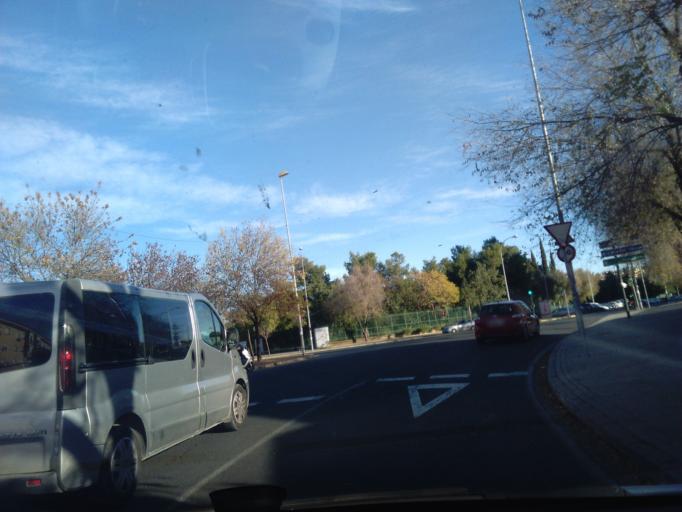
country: ES
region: Andalusia
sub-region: Provincia de Sevilla
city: Sevilla
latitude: 37.3801
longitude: -5.9545
